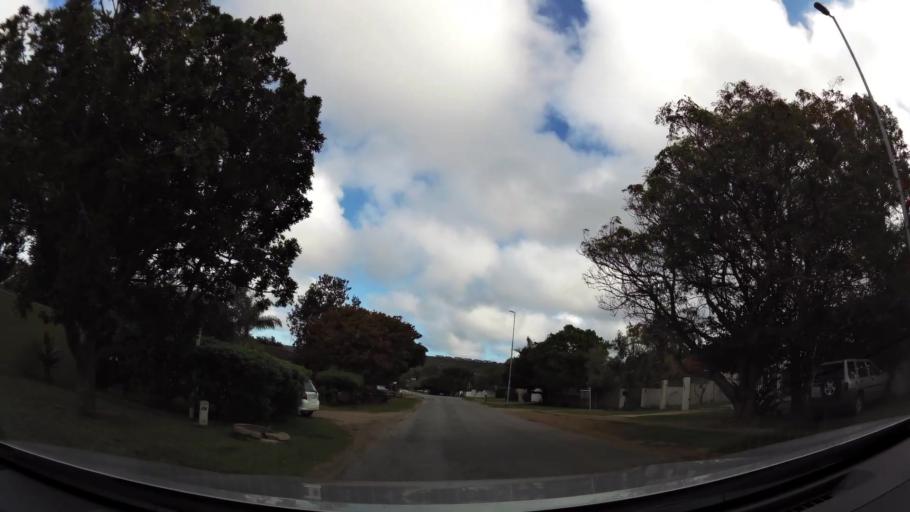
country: ZA
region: Western Cape
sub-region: Eden District Municipality
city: Plettenberg Bay
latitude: -34.0788
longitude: 23.3641
